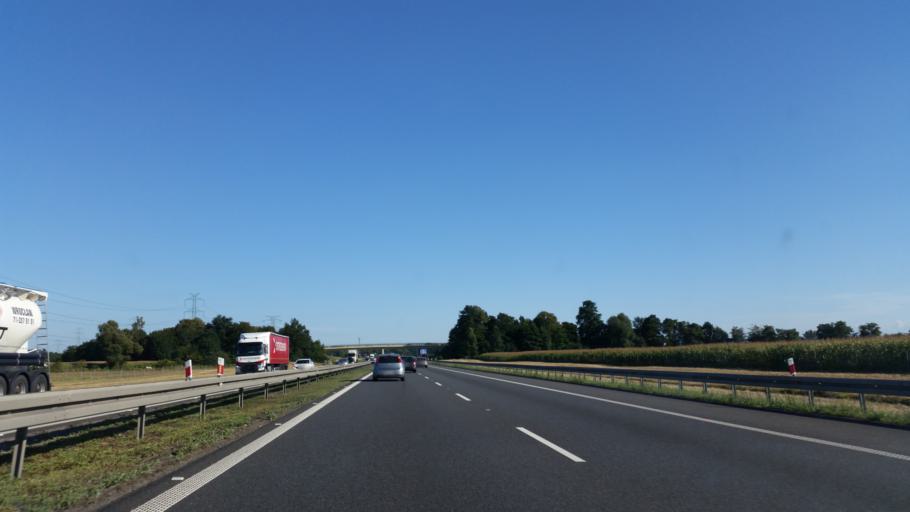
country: PL
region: Lower Silesian Voivodeship
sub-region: Powiat strzelinski
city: Wiazow
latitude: 50.8601
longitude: 17.2239
